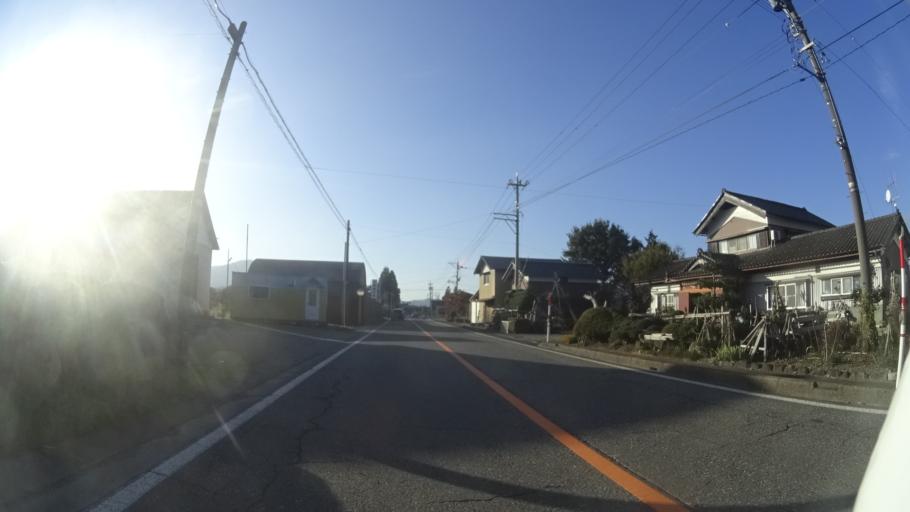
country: JP
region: Fukui
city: Ono
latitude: 35.9784
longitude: 136.5370
